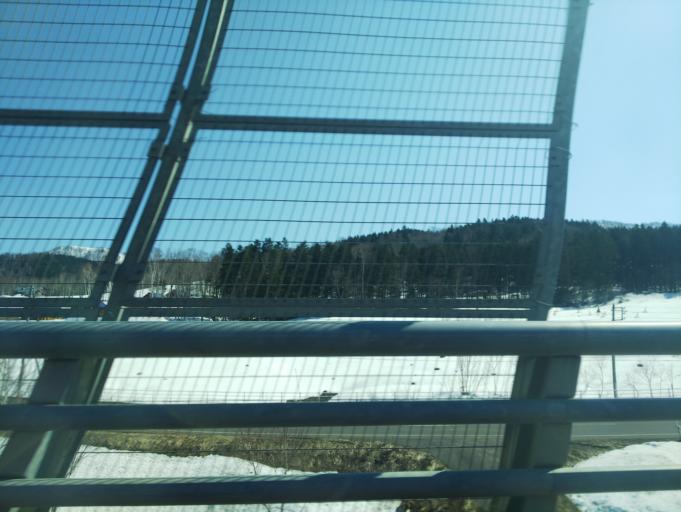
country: JP
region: Hokkaido
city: Nayoro
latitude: 44.7202
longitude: 142.2706
